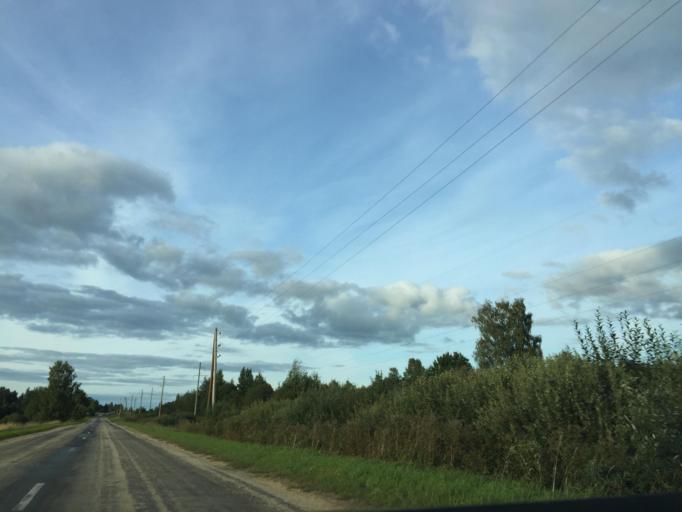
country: LV
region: Nereta
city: Nereta
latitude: 56.2387
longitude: 25.3278
